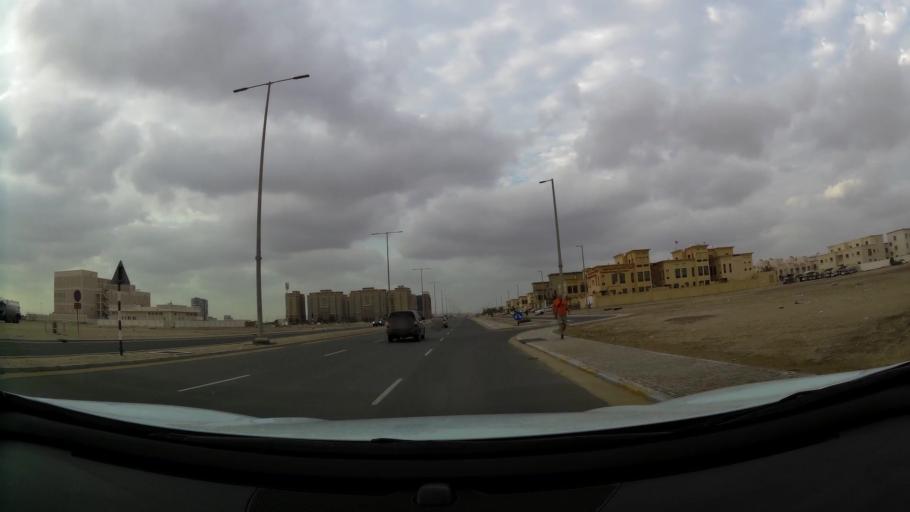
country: AE
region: Abu Dhabi
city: Abu Dhabi
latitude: 24.3646
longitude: 54.5400
